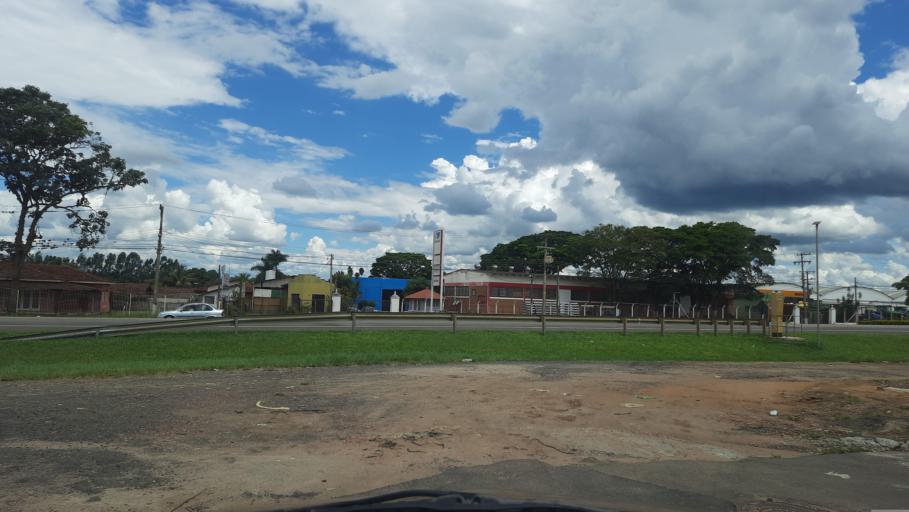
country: BR
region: Sao Paulo
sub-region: Casa Branca
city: Casa Branca
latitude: -21.7819
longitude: -47.0633
